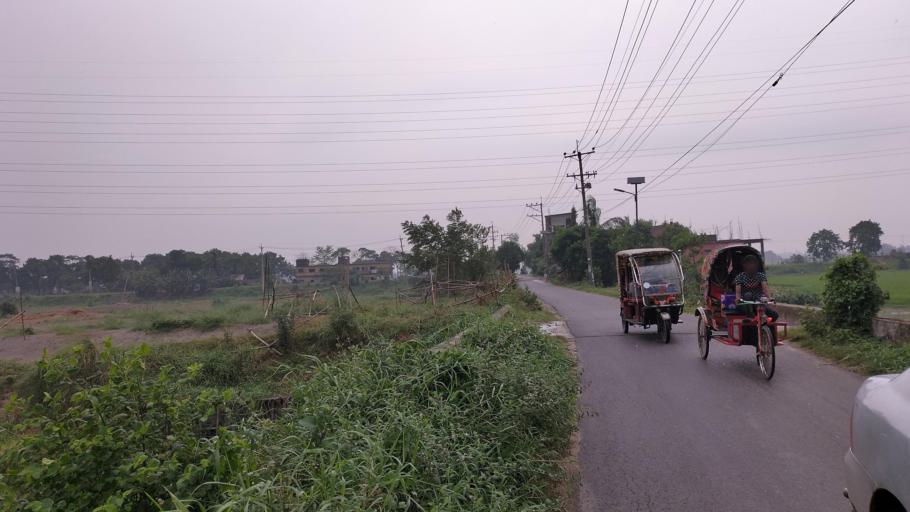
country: BD
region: Dhaka
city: Azimpur
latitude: 23.6830
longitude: 90.3502
